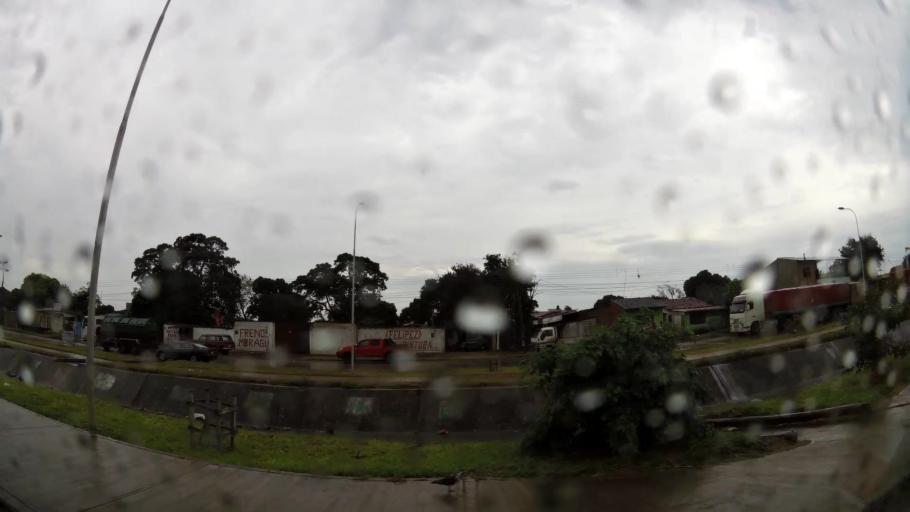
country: BO
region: Santa Cruz
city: Santa Cruz de la Sierra
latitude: -17.8120
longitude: -63.1357
